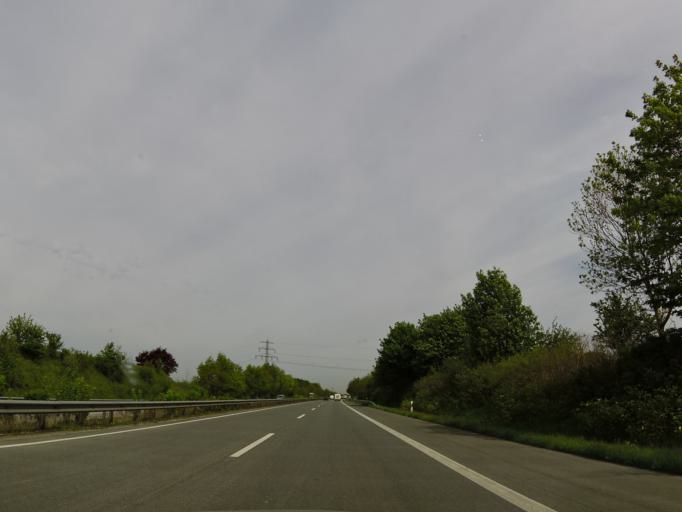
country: DE
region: Schleswig-Holstein
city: Kolln-Reisiek
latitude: 53.7574
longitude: 9.7086
